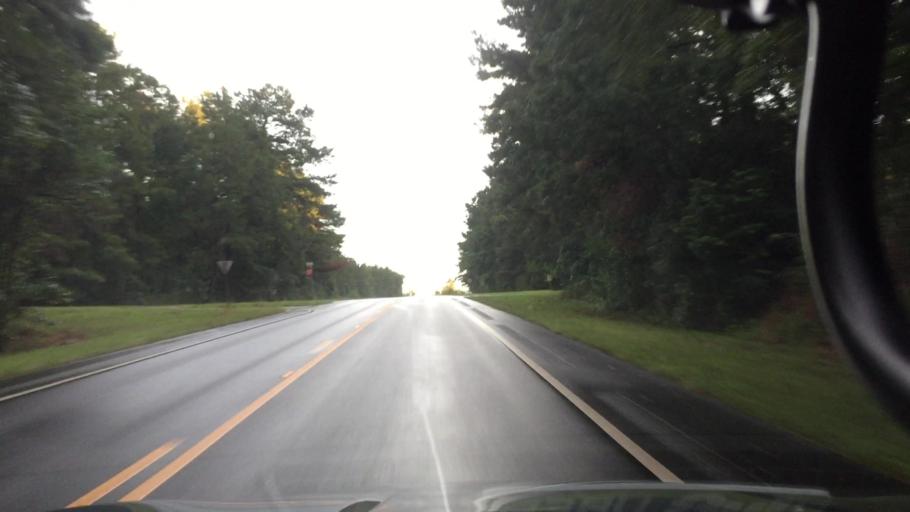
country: US
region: Alabama
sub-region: Coffee County
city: New Brockton
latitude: 31.5500
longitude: -85.9198
